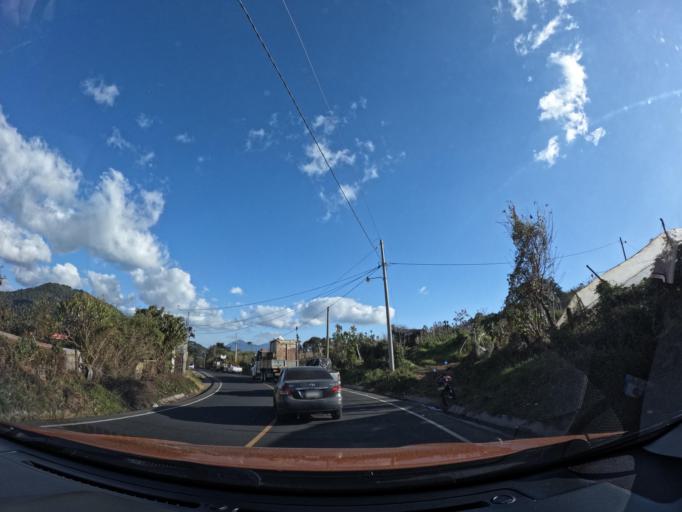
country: GT
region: Sacatepequez
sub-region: Municipio de Santa Maria de Jesus
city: Santa Maria de Jesus
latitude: 14.4858
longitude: -90.7054
